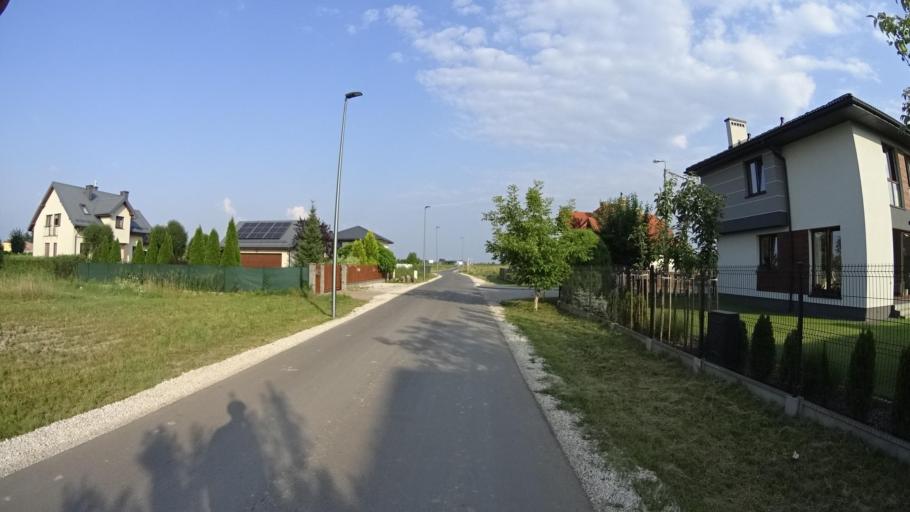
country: PL
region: Masovian Voivodeship
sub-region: Powiat pruszkowski
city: Nowe Grocholice
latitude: 52.1671
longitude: 20.9005
